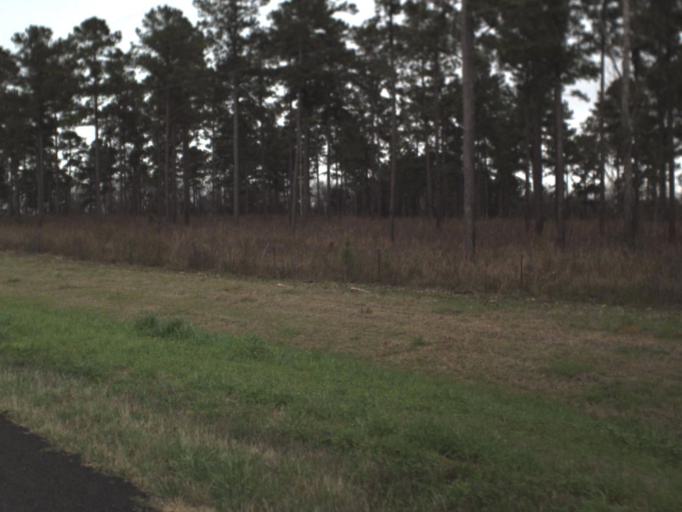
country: US
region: Florida
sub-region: Jefferson County
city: Monticello
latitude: 30.3982
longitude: -83.8772
